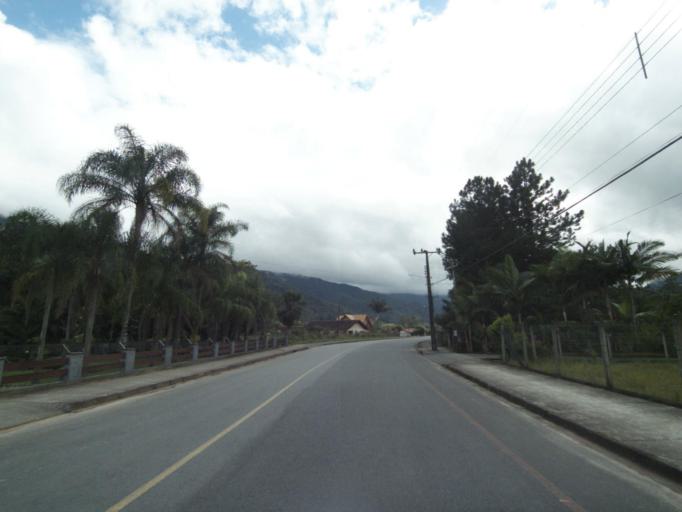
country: BR
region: Santa Catarina
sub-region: Pomerode
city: Pomerode
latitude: -26.6762
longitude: -49.1842
